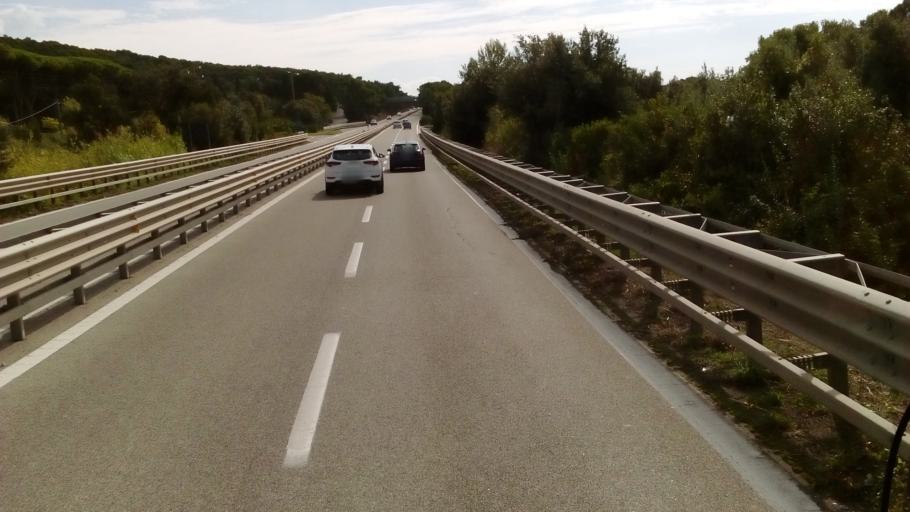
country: IT
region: Tuscany
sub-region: Provincia di Livorno
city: Quercianella
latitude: 43.4398
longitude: 10.3872
